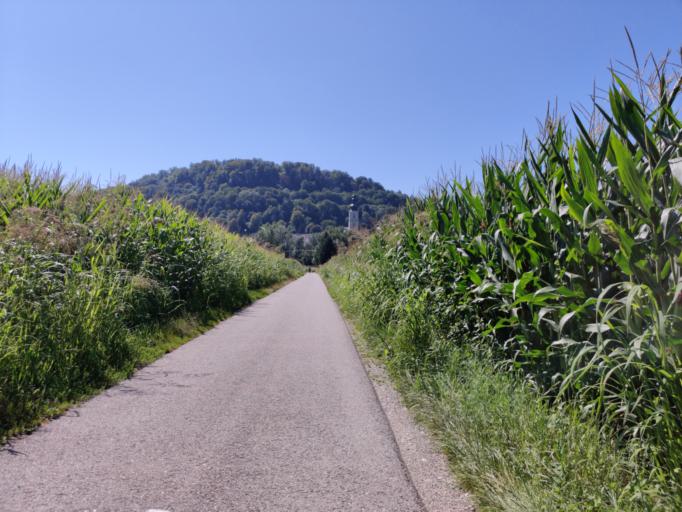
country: AT
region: Styria
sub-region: Politischer Bezirk Leibnitz
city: Wildon
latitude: 46.8916
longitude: 15.5068
